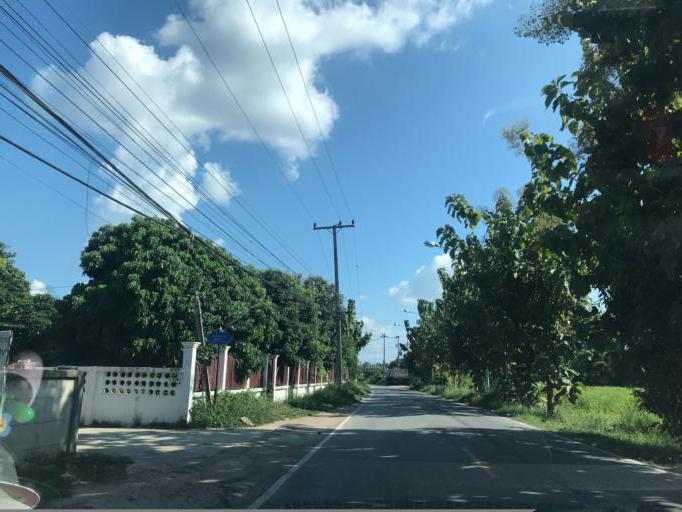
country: TH
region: Lamphun
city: Pa Sang
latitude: 18.5330
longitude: 98.8429
